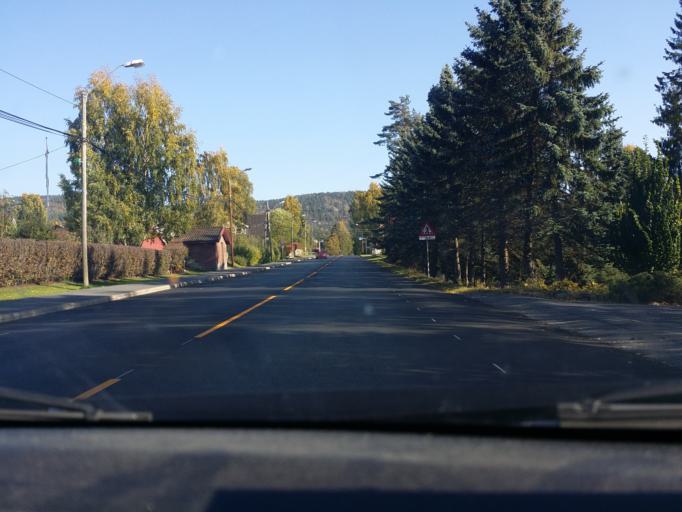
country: NO
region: Akershus
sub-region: Baerum
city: Skui
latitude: 59.9236
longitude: 10.4752
